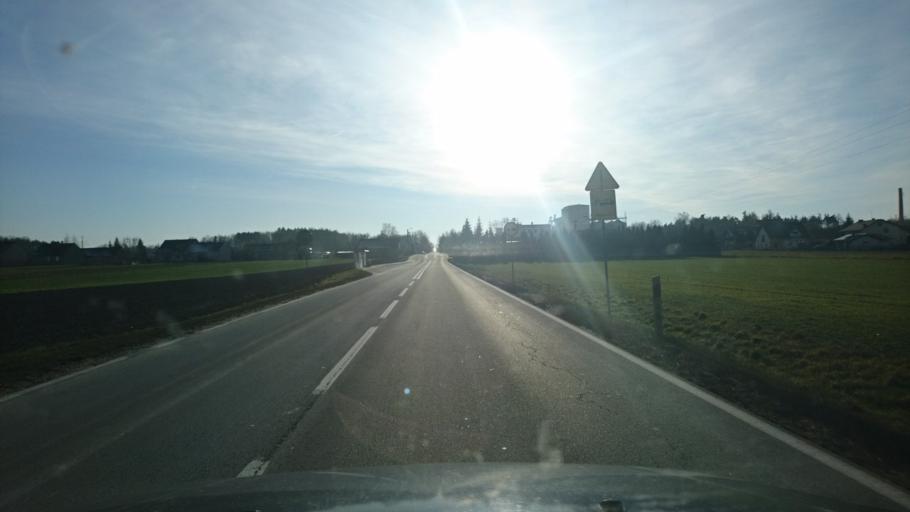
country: PL
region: Opole Voivodeship
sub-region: Powiat oleski
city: Dalachow
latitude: 51.0775
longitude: 18.6029
